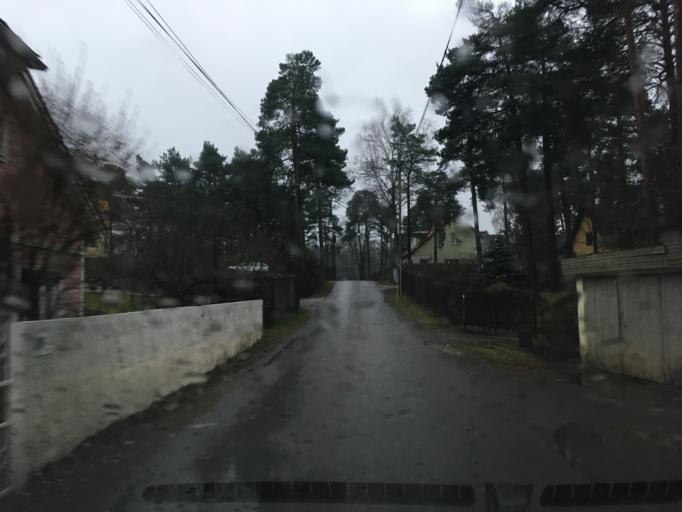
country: EE
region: Harju
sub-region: Tallinna linn
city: Tallinn
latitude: 59.3887
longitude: 24.6947
